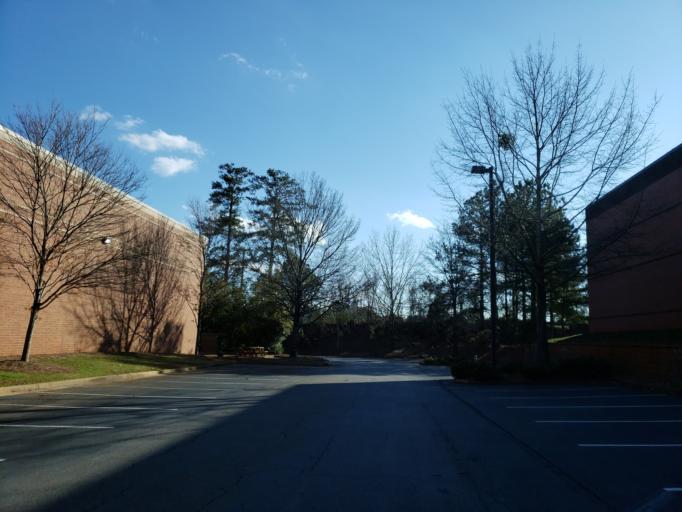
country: US
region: Georgia
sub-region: Cobb County
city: Marietta
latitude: 33.9848
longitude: -84.5206
